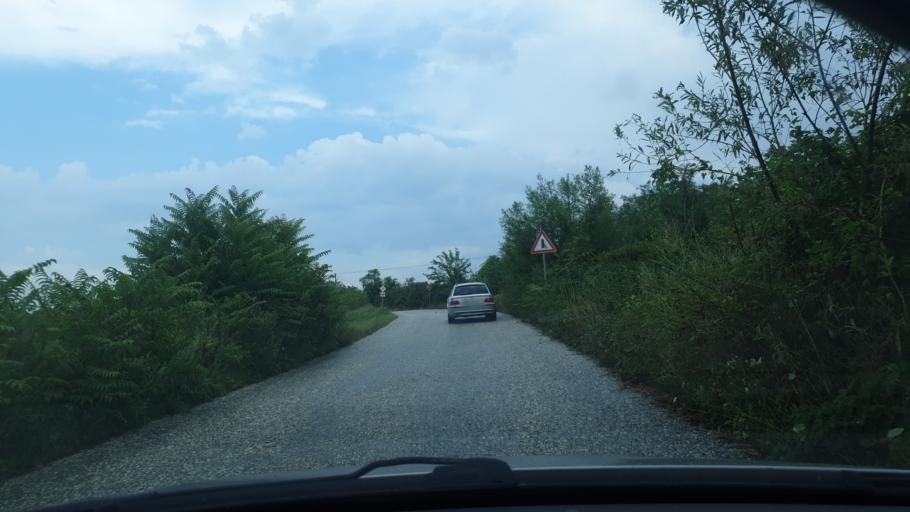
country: RS
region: Central Serbia
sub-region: Sumadijski Okrug
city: Kragujevac
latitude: 44.0674
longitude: 20.7936
